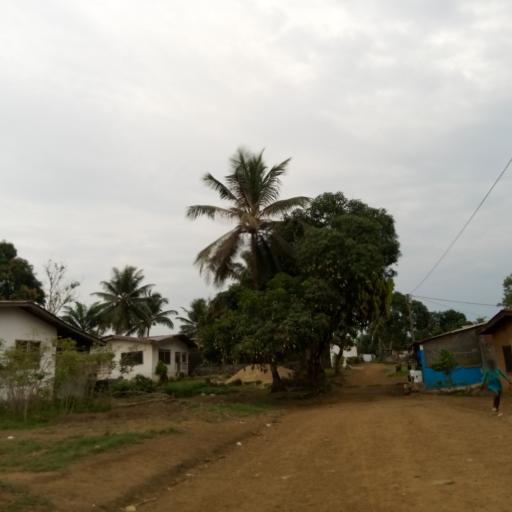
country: LR
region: Montserrado
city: Monrovia
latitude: 6.2932
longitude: -10.6780
